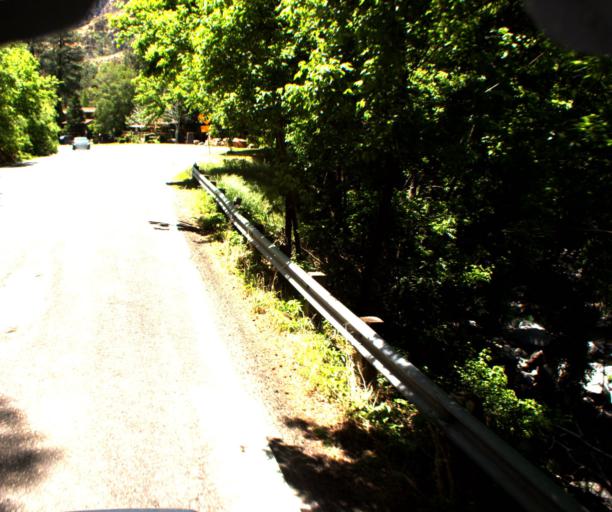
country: US
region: Arizona
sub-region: Coconino County
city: Sedona
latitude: 34.9652
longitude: -111.7515
